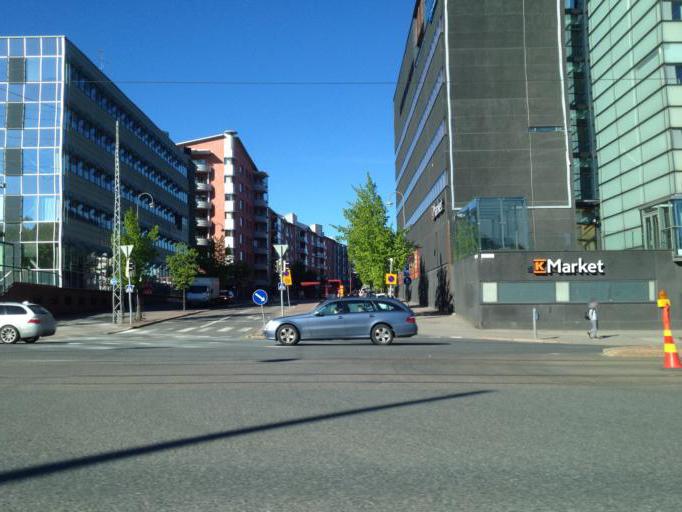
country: FI
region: Uusimaa
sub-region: Helsinki
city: Helsinki
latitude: 60.1947
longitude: 24.8910
